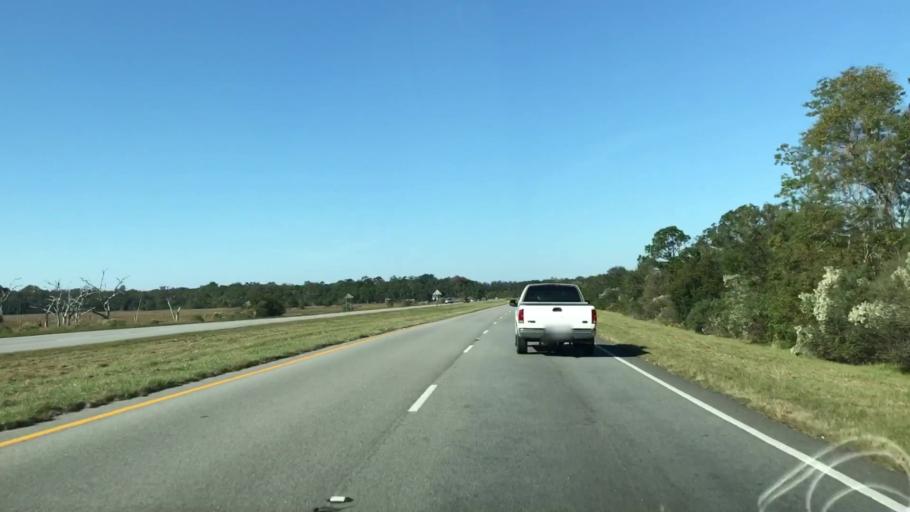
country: US
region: South Carolina
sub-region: Hampton County
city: Yemassee
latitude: 32.5995
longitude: -80.7716
